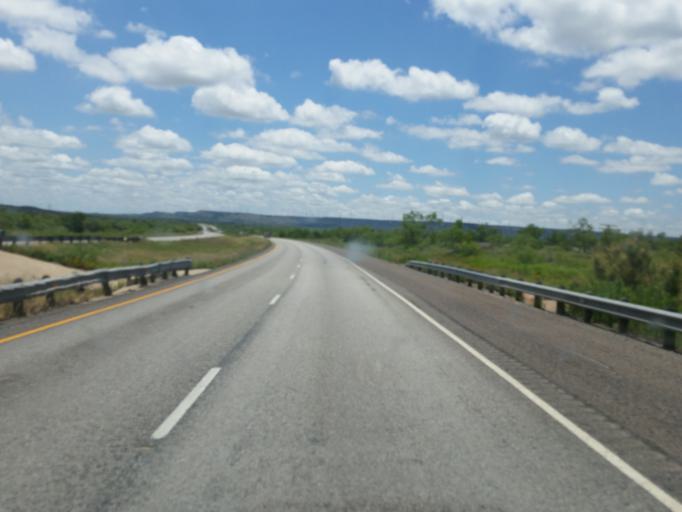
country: US
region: Texas
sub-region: Garza County
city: Post
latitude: 33.0149
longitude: -101.1770
